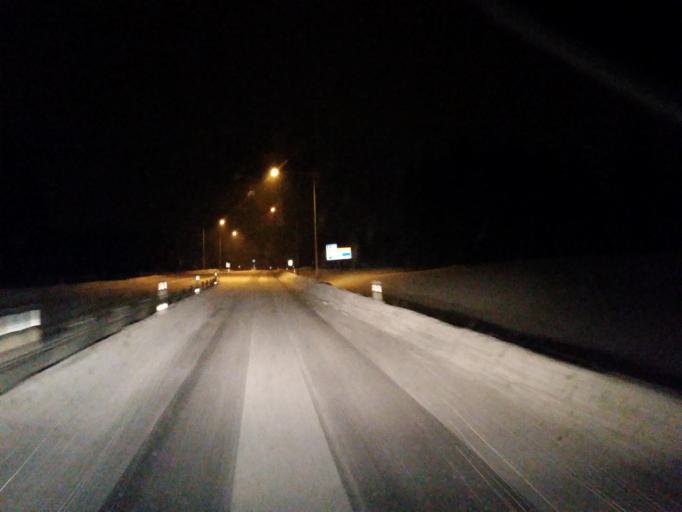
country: SE
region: Norrbotten
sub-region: Pitea Kommun
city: Pitea
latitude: 65.2784
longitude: 21.4481
